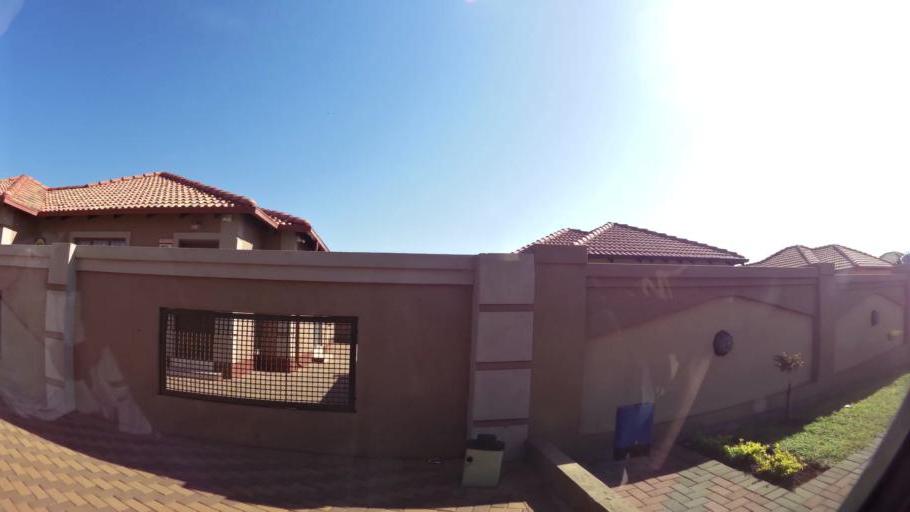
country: ZA
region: North-West
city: Ga-Rankuwa
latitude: -25.6387
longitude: 28.0763
